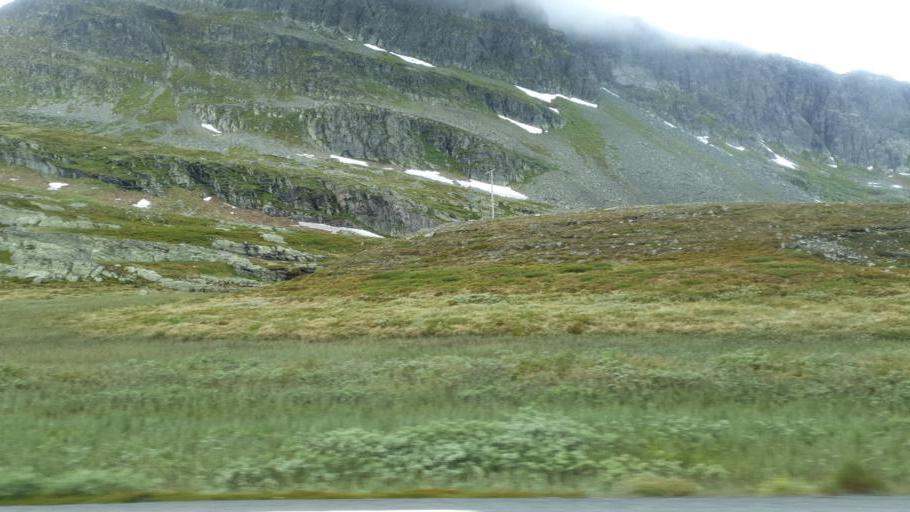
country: NO
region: Oppland
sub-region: Vestre Slidre
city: Slidre
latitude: 61.2952
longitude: 8.8140
